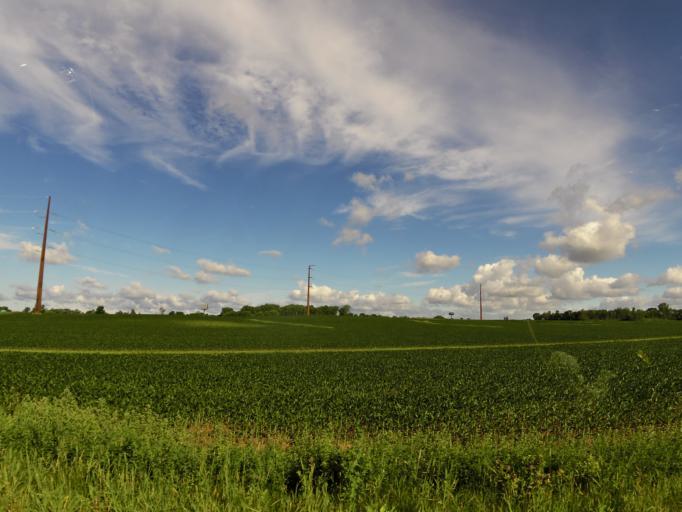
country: US
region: Minnesota
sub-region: Goodhue County
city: Cannon Falls
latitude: 44.6017
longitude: -92.9885
